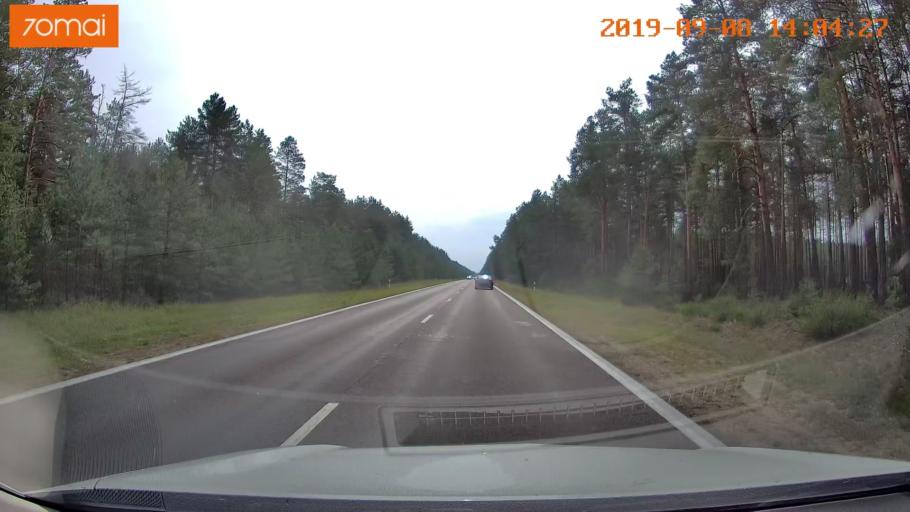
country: LT
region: Alytaus apskritis
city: Druskininkai
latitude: 54.0981
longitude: 24.2005
